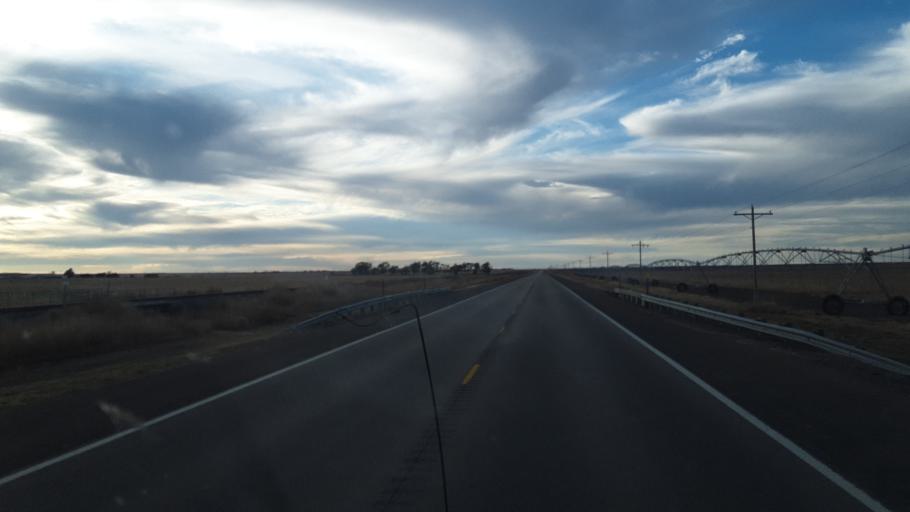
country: US
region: Kansas
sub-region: Hamilton County
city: Syracuse
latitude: 38.0025
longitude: -101.8383
